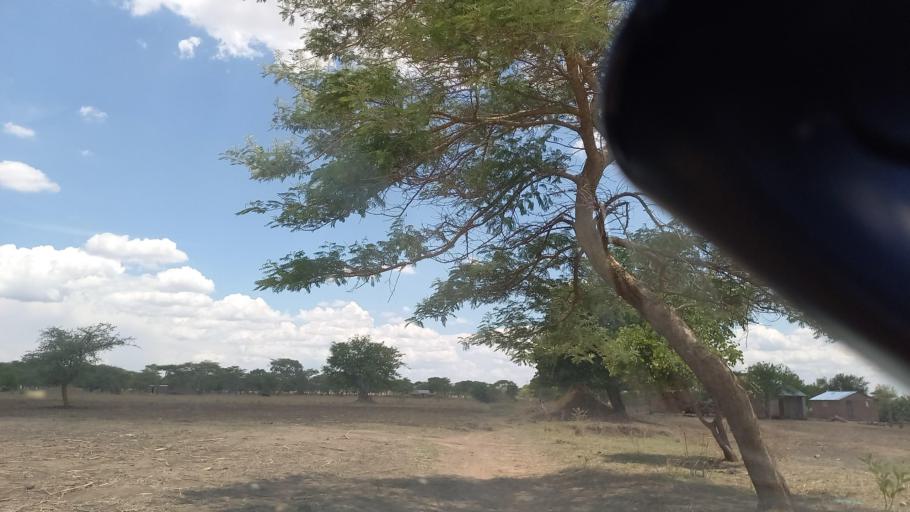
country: ZM
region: Southern
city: Mazabuka
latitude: -16.1218
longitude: 27.7769
